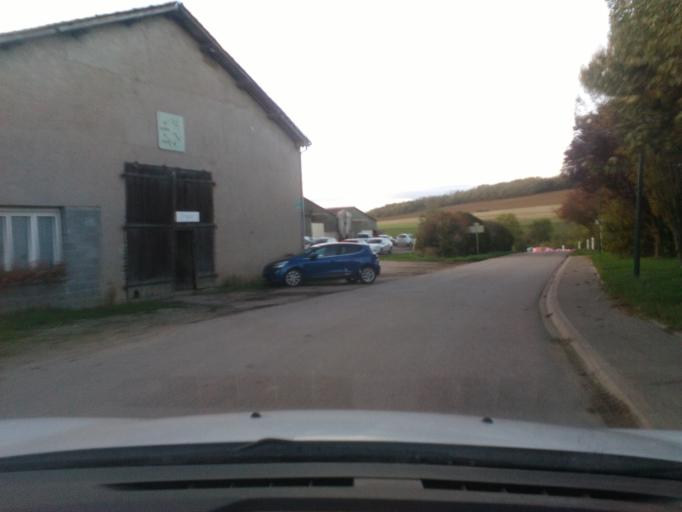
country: FR
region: Lorraine
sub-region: Departement des Vosges
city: Mirecourt
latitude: 48.3994
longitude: 6.1652
